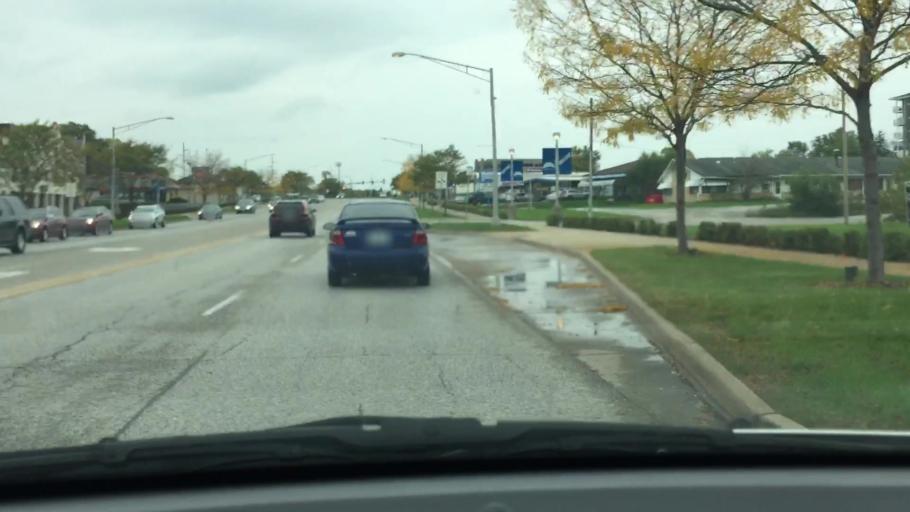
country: US
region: Iowa
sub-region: Johnson County
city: Coralville
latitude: 41.6718
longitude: -91.5746
